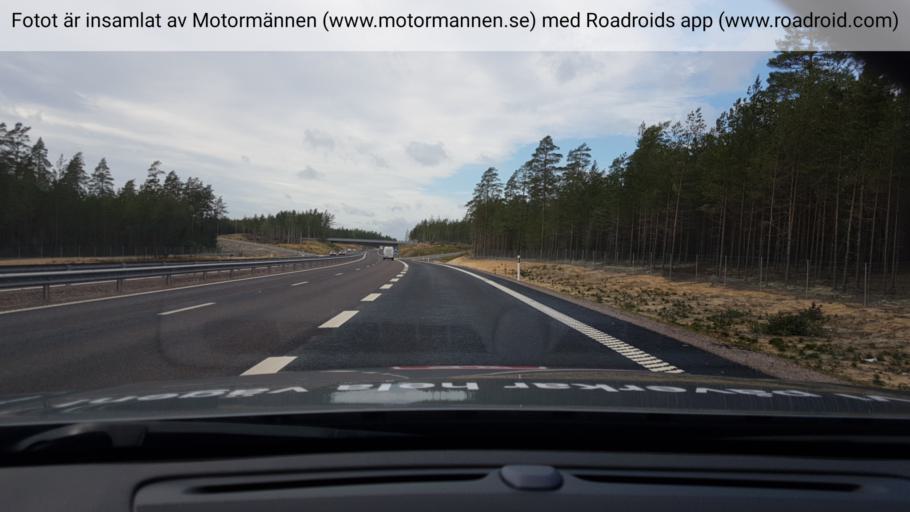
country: SE
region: Vaermland
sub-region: Kils Kommun
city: Kil
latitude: 59.3851
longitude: 13.3445
